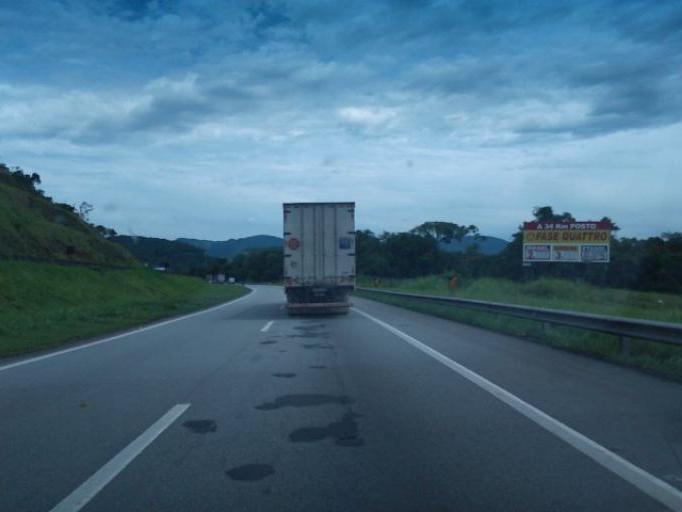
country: BR
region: Sao Paulo
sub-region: Miracatu
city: Miracatu
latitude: -24.2081
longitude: -47.3721
